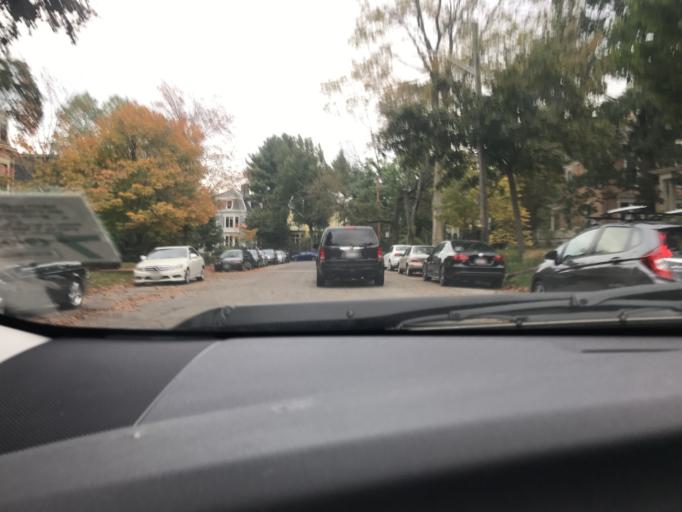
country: US
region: Massachusetts
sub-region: Middlesex County
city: Cambridge
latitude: 42.3870
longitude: -71.1225
